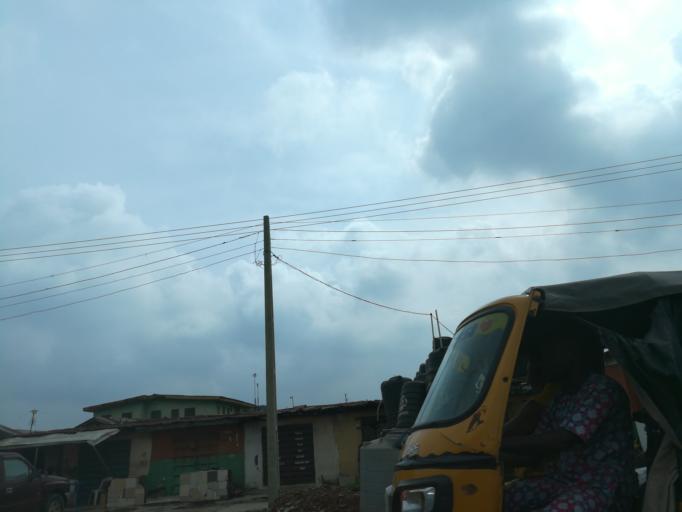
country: NG
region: Lagos
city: Agege
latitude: 6.5855
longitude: 3.3061
